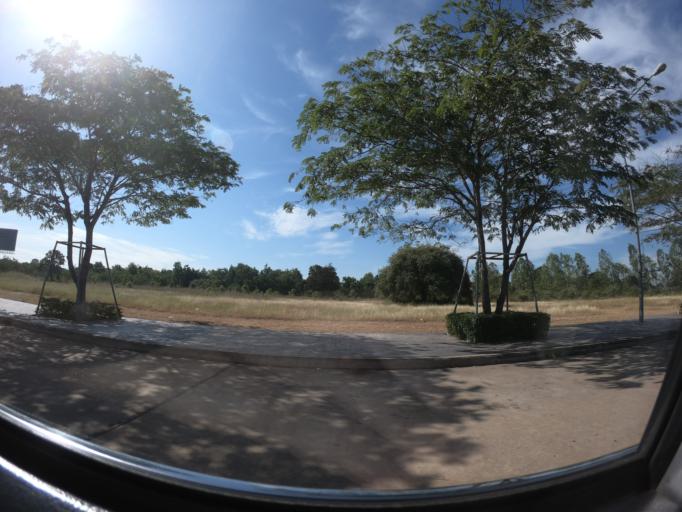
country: TH
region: Khon Kaen
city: Khon Kaen
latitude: 16.3887
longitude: 102.8086
